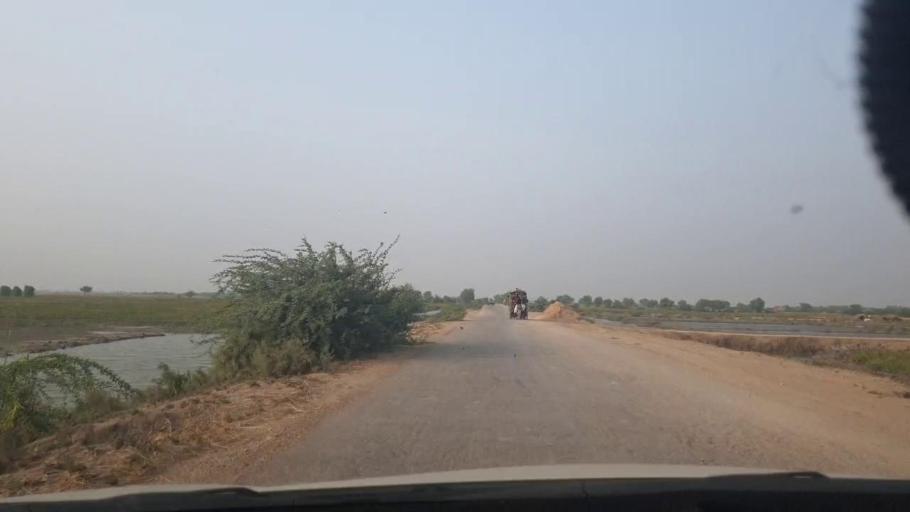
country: PK
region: Sindh
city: Bulri
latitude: 24.7791
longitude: 68.4198
